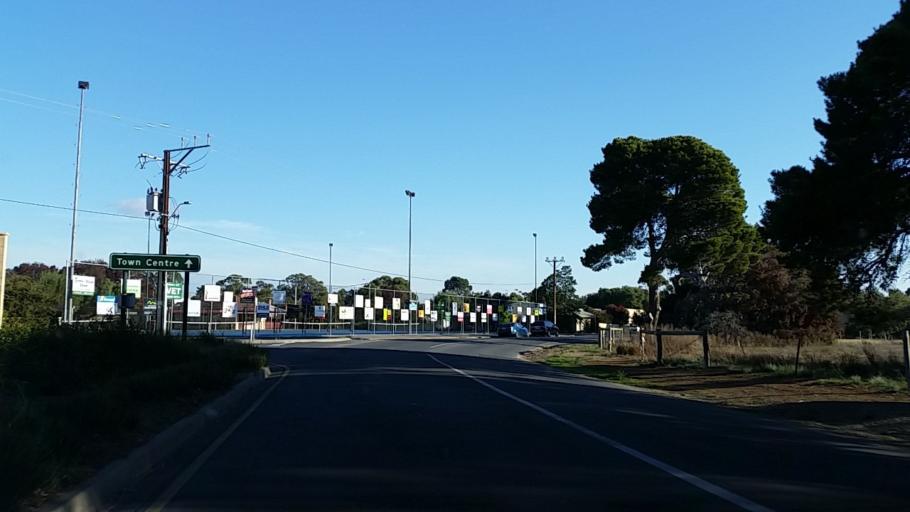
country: AU
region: South Australia
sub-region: Alexandrina
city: Strathalbyn
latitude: -35.2517
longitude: 138.8937
